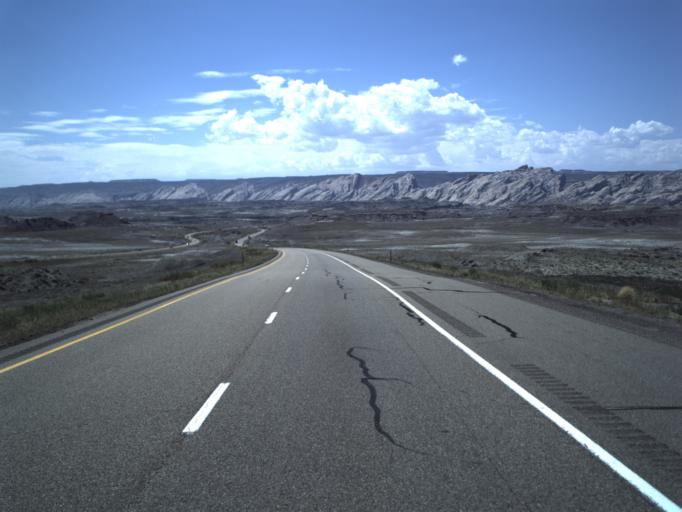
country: US
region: Utah
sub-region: Carbon County
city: East Carbon City
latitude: 38.9393
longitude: -110.3408
